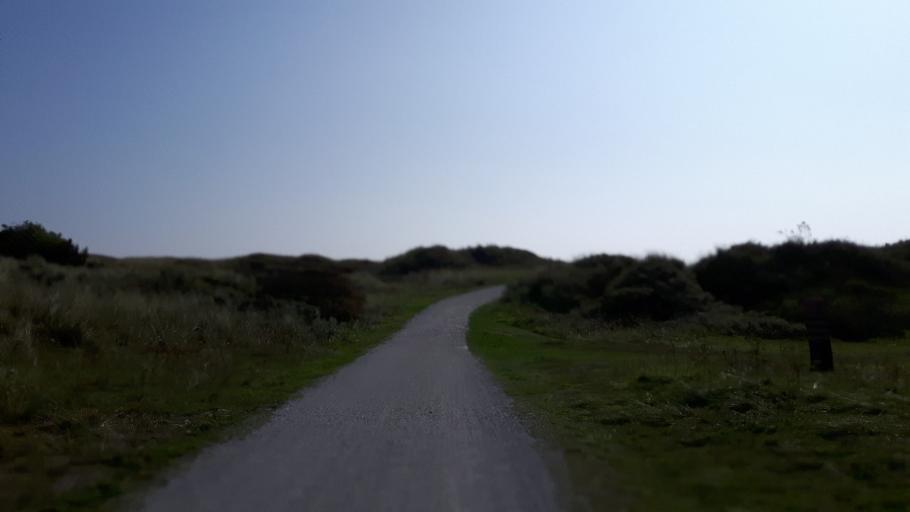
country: NL
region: Friesland
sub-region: Gemeente Ameland
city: Nes
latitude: 53.4590
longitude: 5.7921
